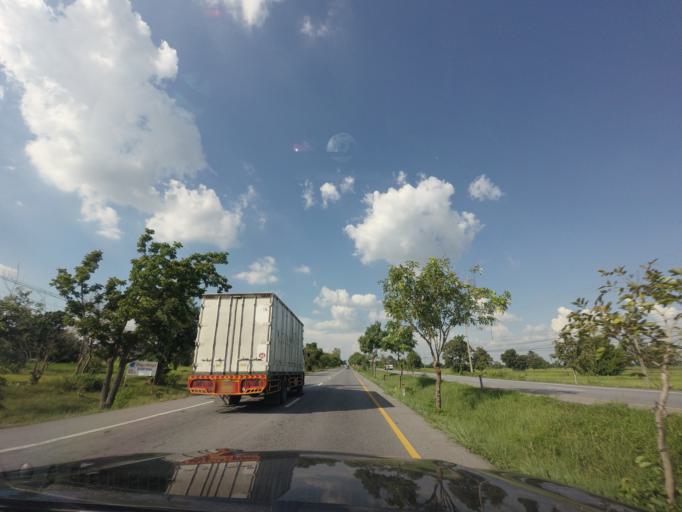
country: TH
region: Khon Kaen
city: Phon
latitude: 15.7153
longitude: 102.5895
